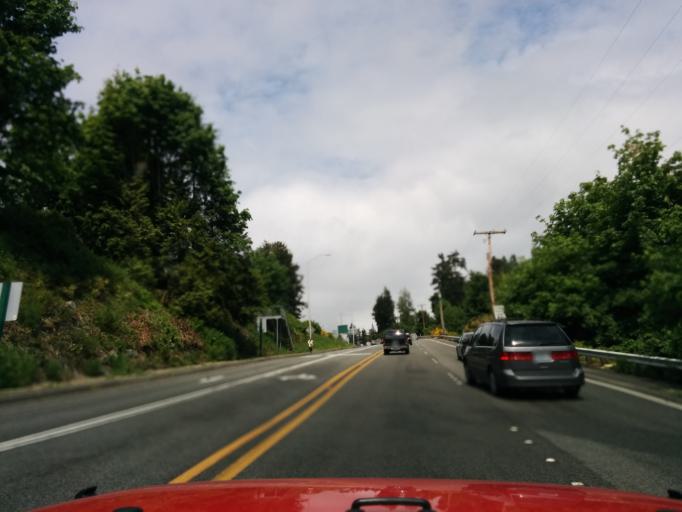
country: US
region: Washington
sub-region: Snohomish County
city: Mukilteo
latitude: 47.9750
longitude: -122.3526
